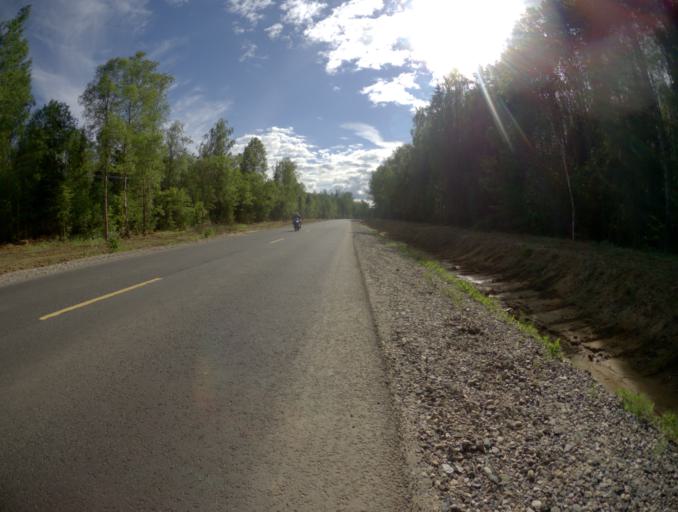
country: RU
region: Ivanovo
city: Kitovo
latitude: 56.8189
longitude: 41.2638
